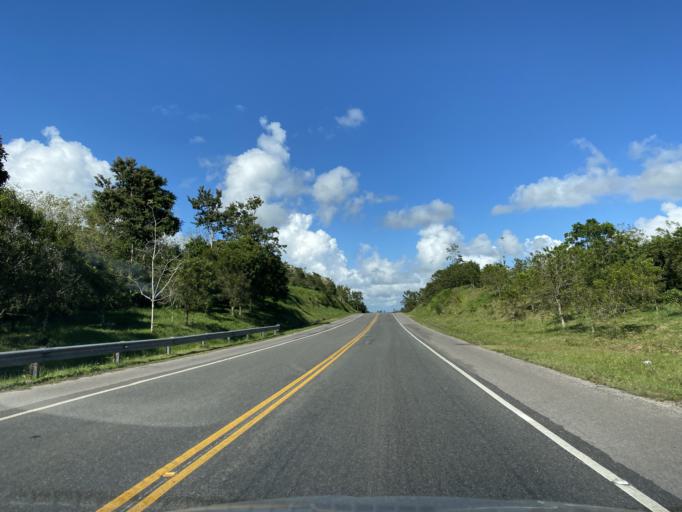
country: DO
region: Monte Plata
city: Majagual
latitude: 19.0162
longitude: -69.8228
